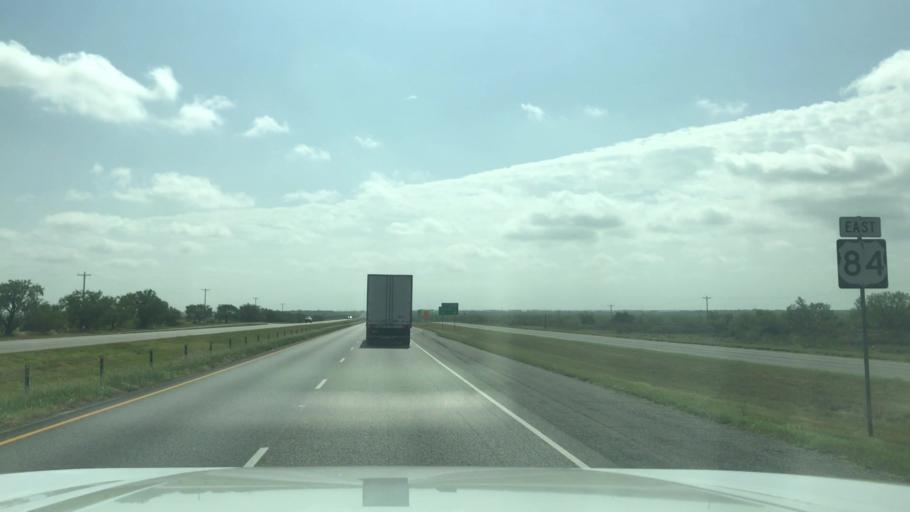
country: US
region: Texas
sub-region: Taylor County
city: Merkel
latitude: 32.4638
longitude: -99.9608
